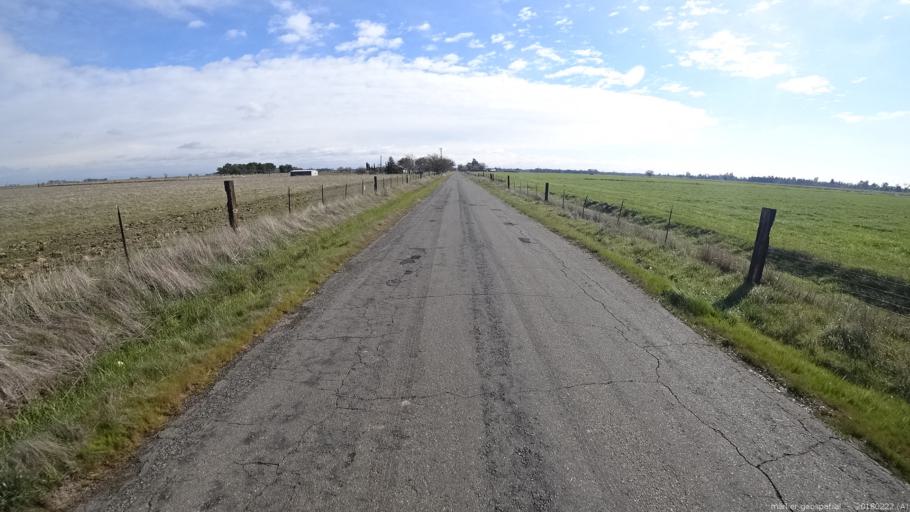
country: US
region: California
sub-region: Sacramento County
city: Elverta
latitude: 38.7290
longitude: -121.4263
